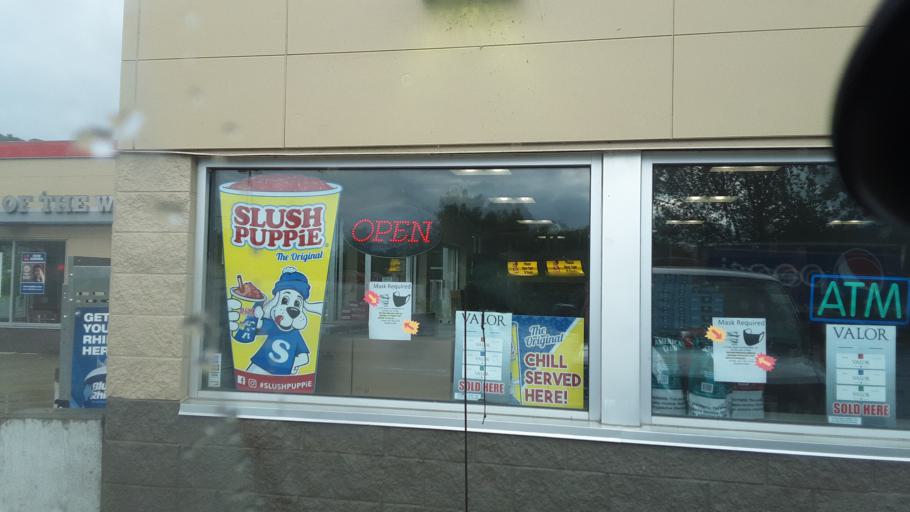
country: US
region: New York
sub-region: Cattaraugus County
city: Salamanca
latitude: 42.1574
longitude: -78.7478
